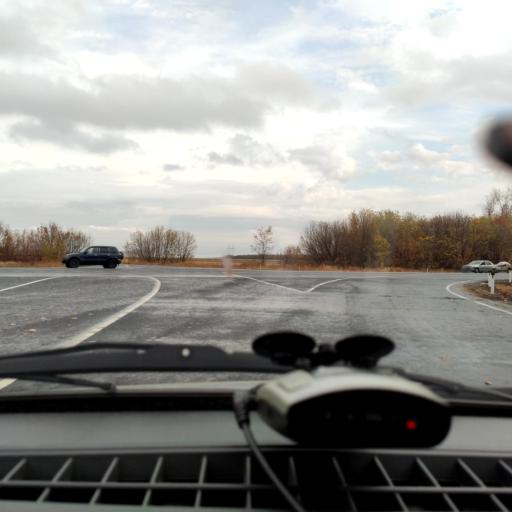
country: RU
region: Voronezj
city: Uryv-Pokrovka
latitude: 51.2299
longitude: 39.0592
